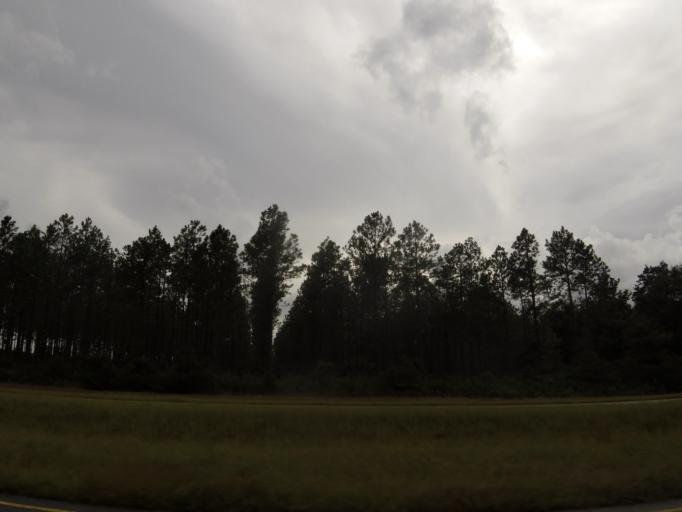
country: US
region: Georgia
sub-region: Wayne County
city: Jesup
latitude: 31.4951
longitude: -81.7490
